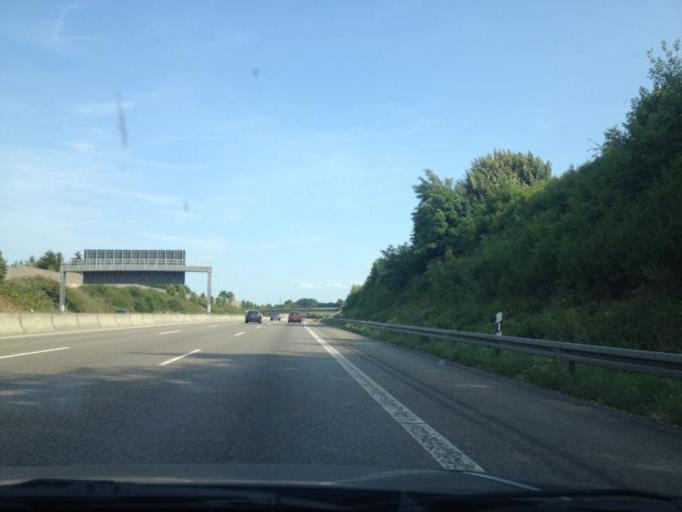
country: DE
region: Baden-Wuerttemberg
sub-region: Karlsruhe Region
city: Sinsheim
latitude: 49.2354
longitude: 8.8997
